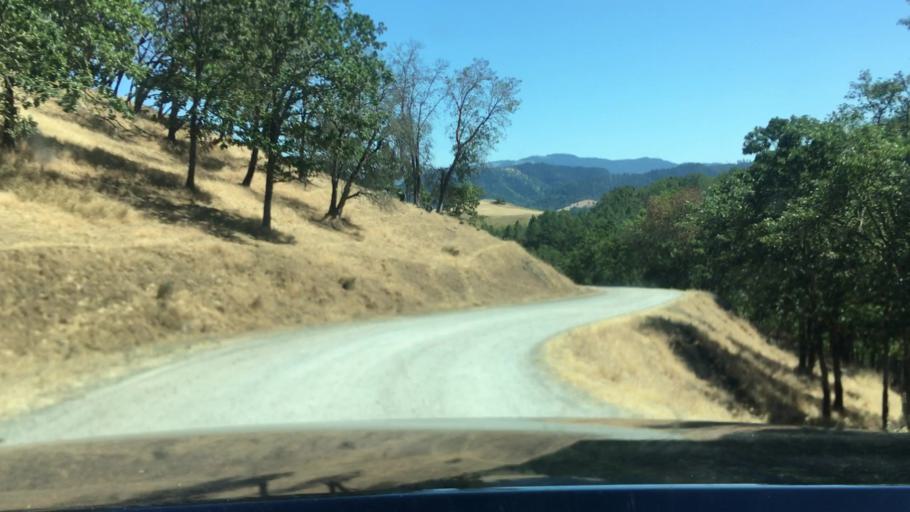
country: US
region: Oregon
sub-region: Douglas County
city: Winston
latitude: 43.1372
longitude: -123.4386
